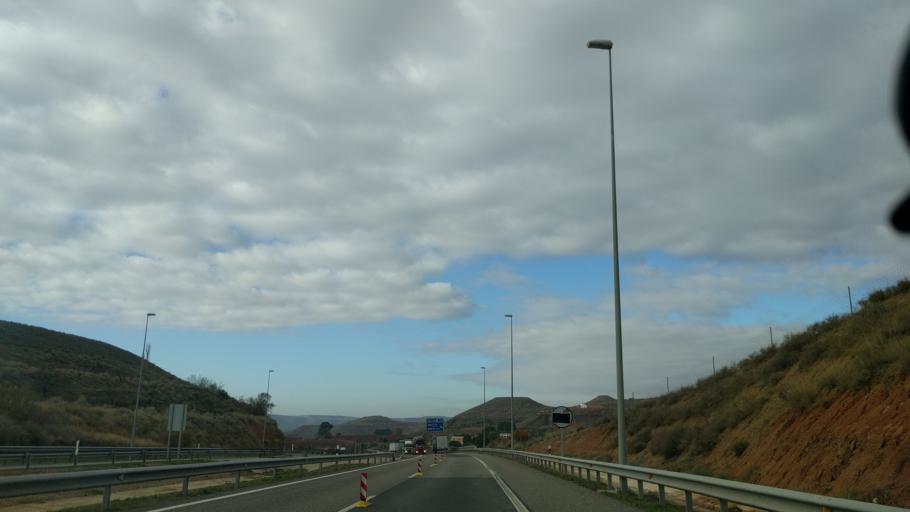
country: ES
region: Aragon
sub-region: Provincia de Huesca
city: Fraga
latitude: 41.5224
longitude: 0.3846
